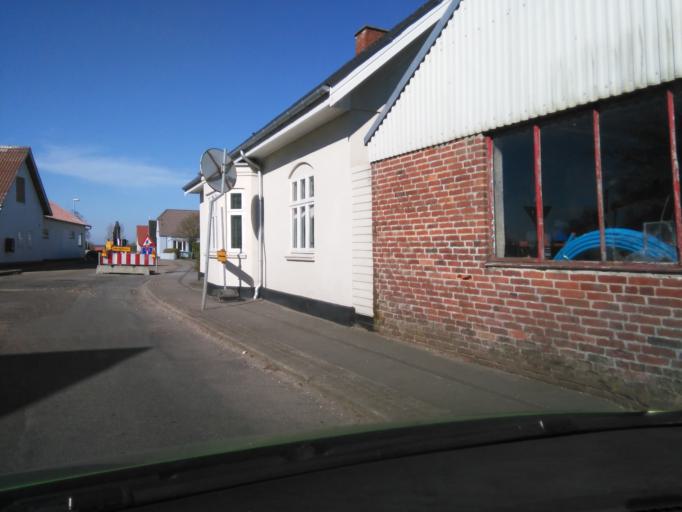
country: DK
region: South Denmark
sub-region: Varde Kommune
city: Oksbol
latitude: 55.6552
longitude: 8.2909
